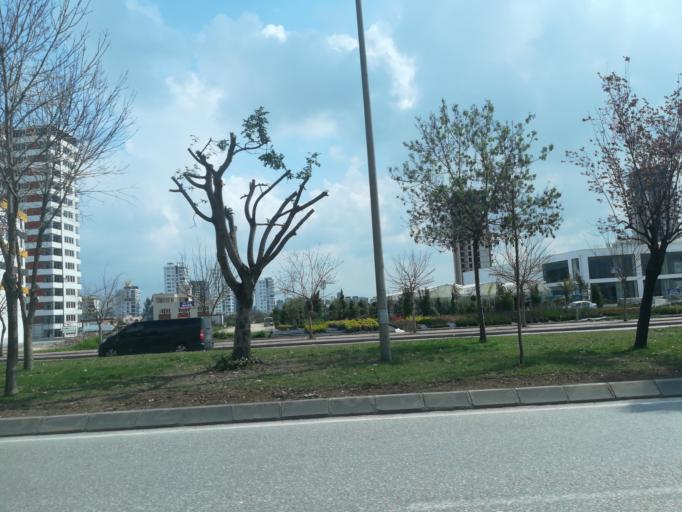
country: TR
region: Adana
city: Seyhan
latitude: 37.0134
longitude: 35.2502
